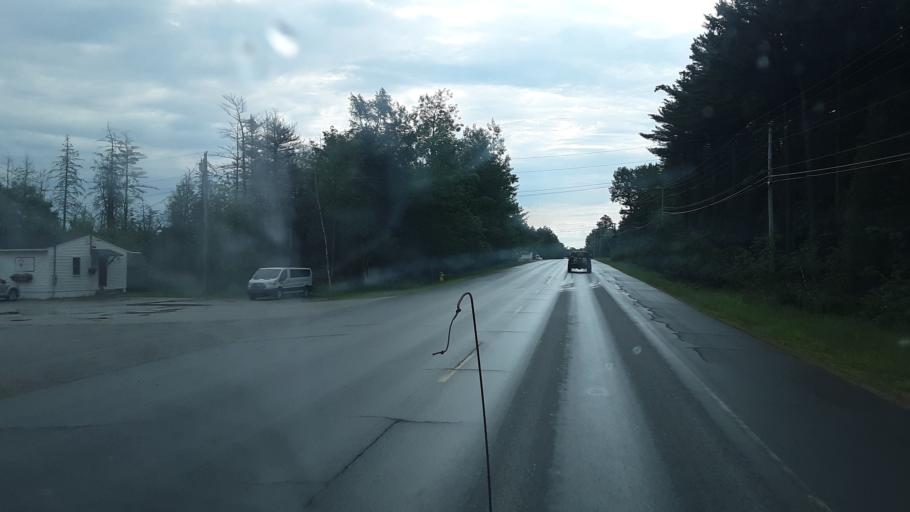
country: US
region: Maine
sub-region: Penobscot County
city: Old Town
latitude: 44.9427
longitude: -68.6701
